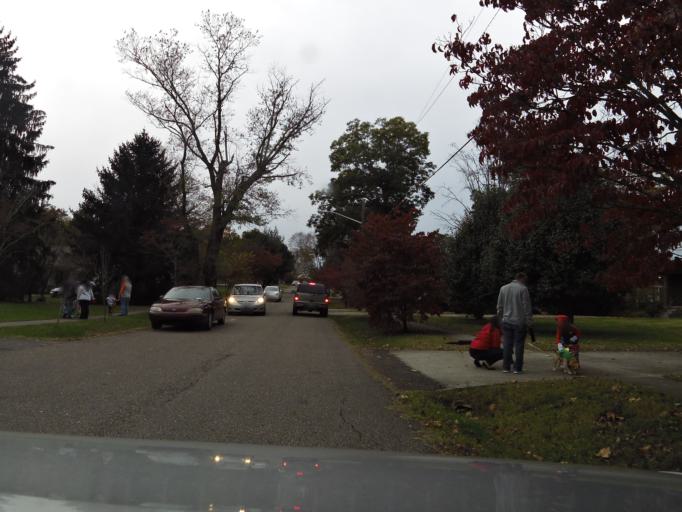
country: US
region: Tennessee
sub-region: Knox County
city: Knoxville
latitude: 36.0371
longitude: -83.9227
